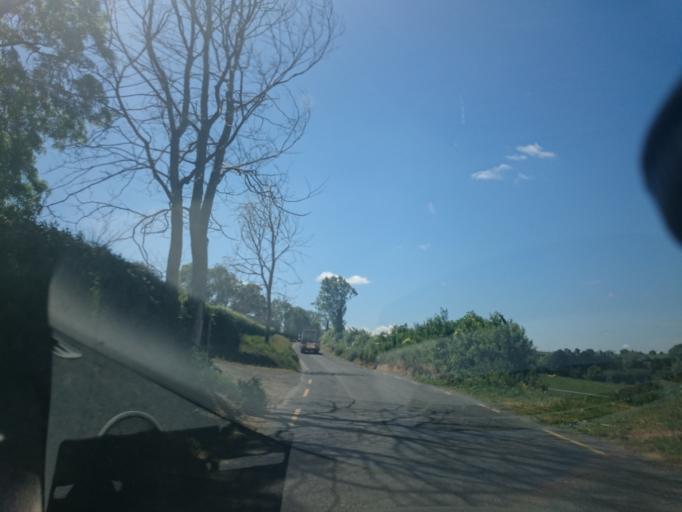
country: IE
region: Leinster
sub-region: Kilkenny
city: Graiguenamanagh
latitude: 52.6125
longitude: -6.9909
